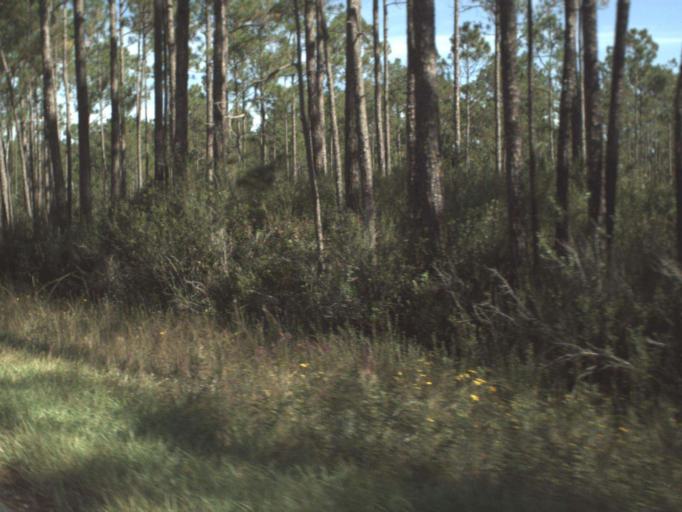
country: US
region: Florida
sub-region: Gulf County
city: Wewahitchka
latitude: 30.0941
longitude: -84.9847
